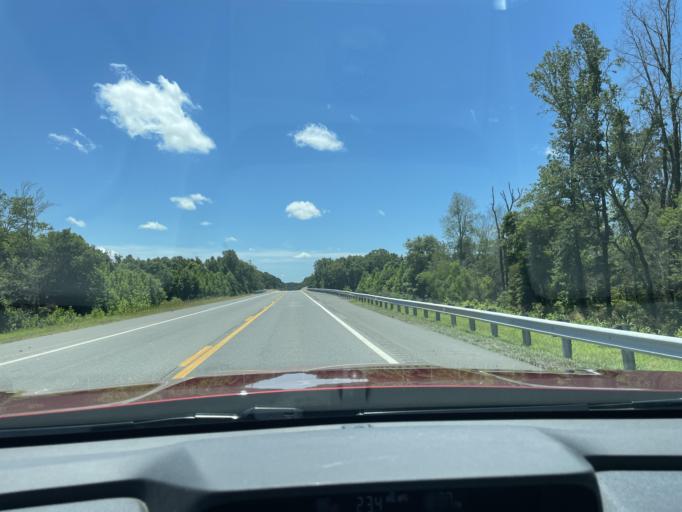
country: US
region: Arkansas
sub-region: Jefferson County
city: Pine Bluff
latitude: 34.1445
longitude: -91.9764
